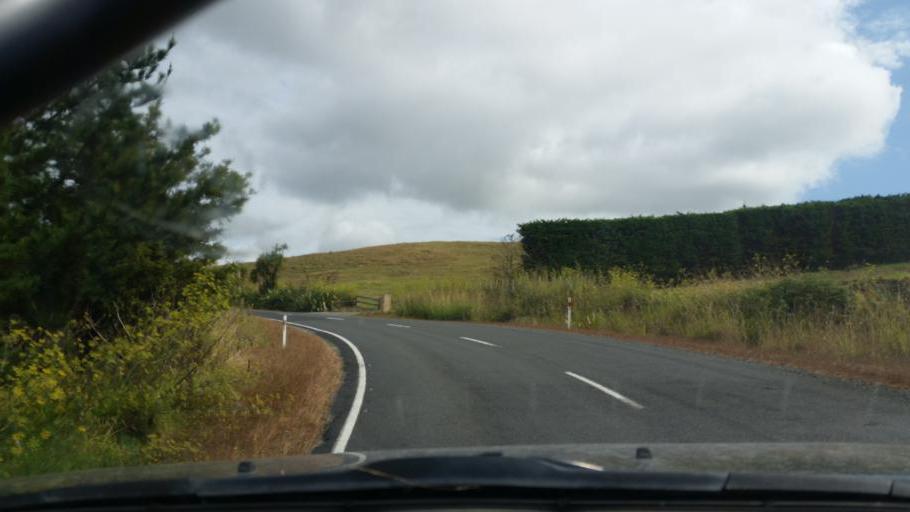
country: NZ
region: Northland
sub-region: Kaipara District
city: Dargaville
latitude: -35.9579
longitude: 173.9246
